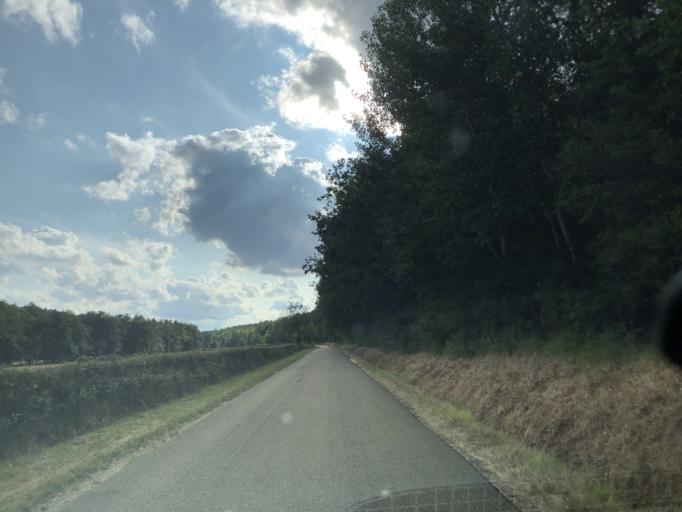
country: FR
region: Bourgogne
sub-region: Departement de l'Yonne
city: Saint-Georges-sur-Baulche
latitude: 47.8230
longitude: 3.5171
